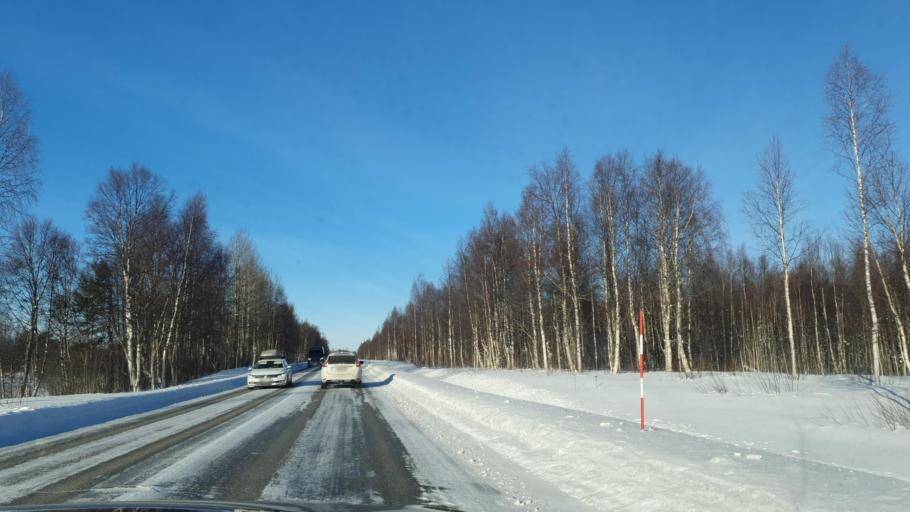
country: SE
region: Norrbotten
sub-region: Overtornea Kommun
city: OEvertornea
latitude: 66.4022
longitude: 23.6774
